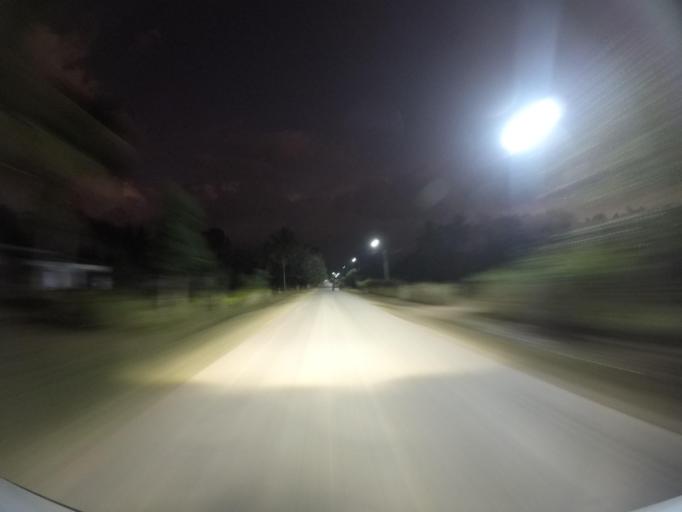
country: TL
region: Lautem
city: Lospalos
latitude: -8.4734
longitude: 126.9929
